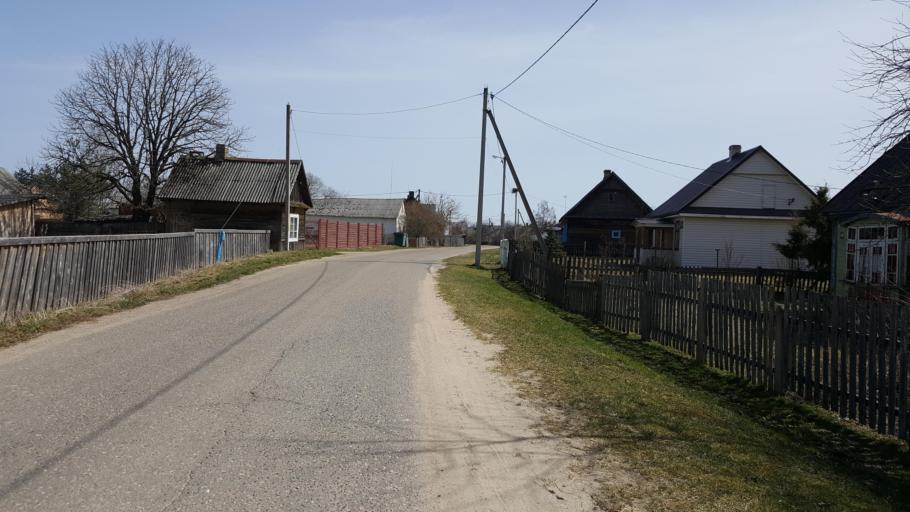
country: BY
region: Brest
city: Kamyanyuki
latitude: 52.5612
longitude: 23.7931
